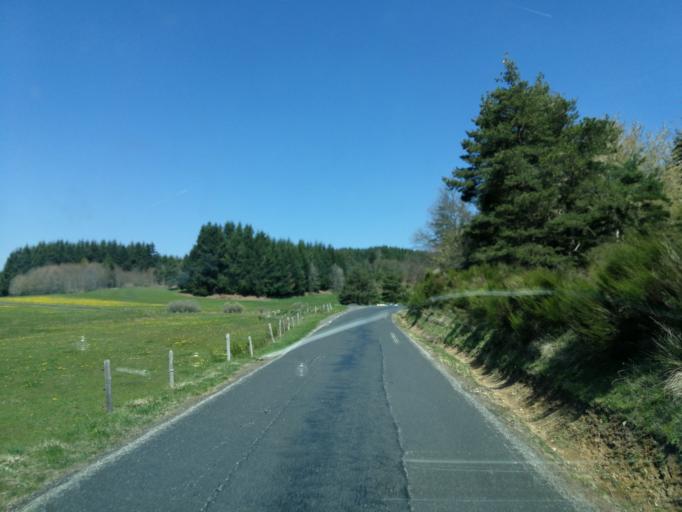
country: FR
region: Rhone-Alpes
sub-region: Departement de l'Ardeche
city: Le Cheylard
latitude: 44.9475
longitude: 4.4185
